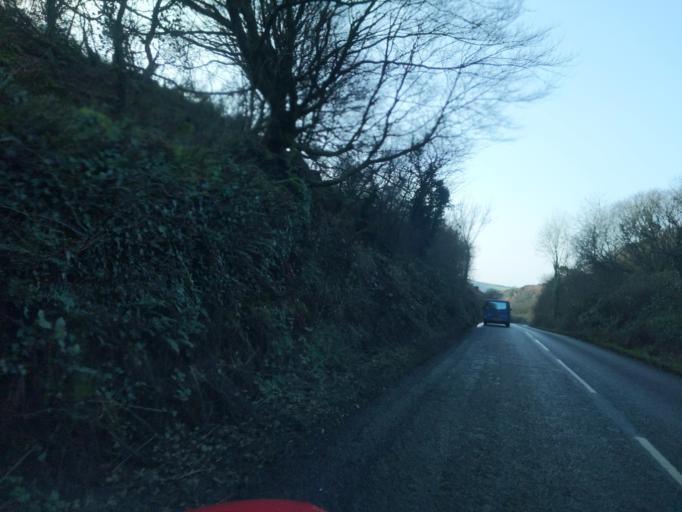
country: GB
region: England
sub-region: Cornwall
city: Tintagel
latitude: 50.6433
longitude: -4.7185
